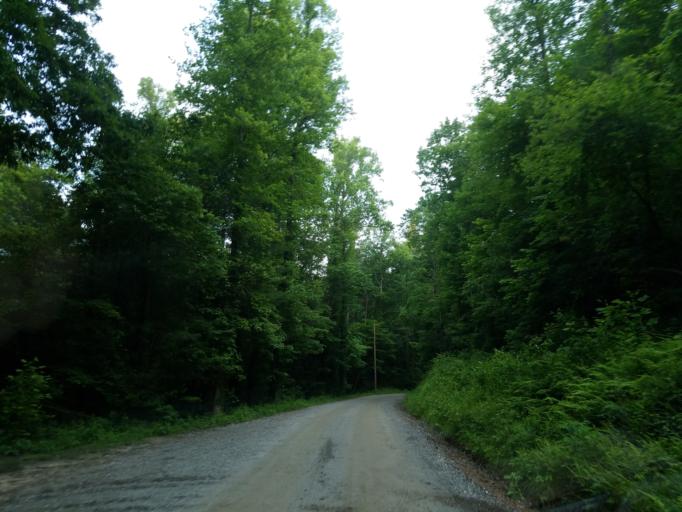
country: US
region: Georgia
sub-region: Dawson County
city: Dawsonville
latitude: 34.5685
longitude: -84.1365
